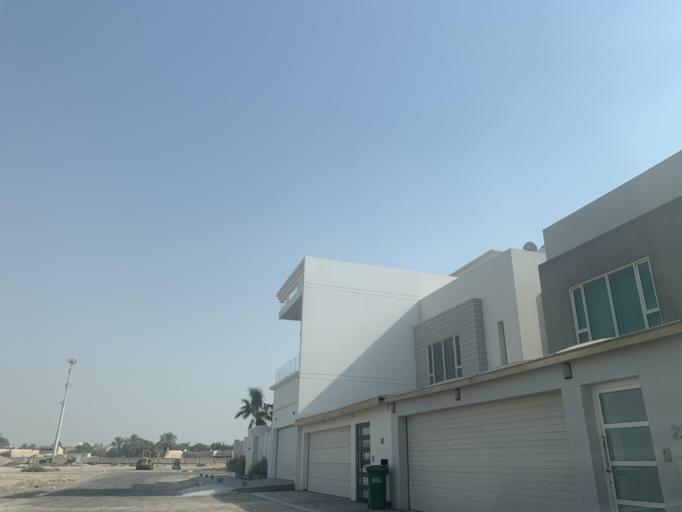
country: BH
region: Manama
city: Jidd Hafs
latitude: 26.2051
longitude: 50.4898
